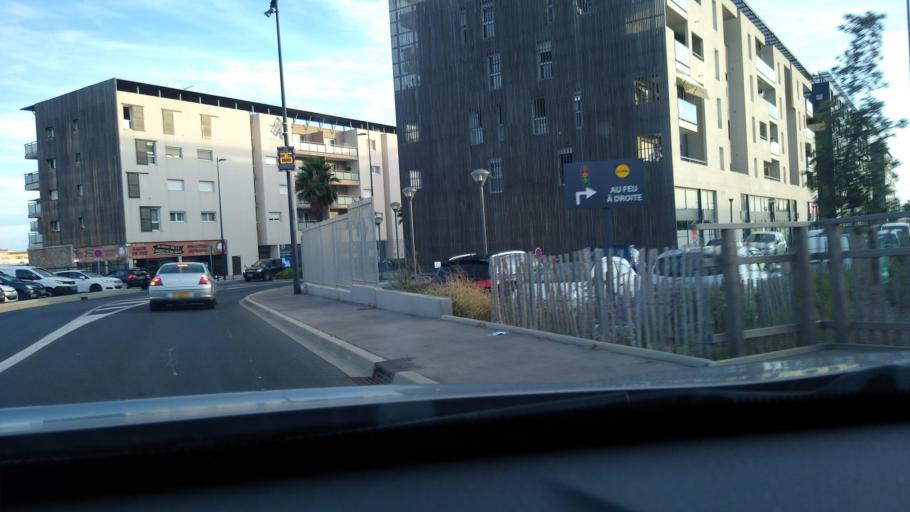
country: FR
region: Languedoc-Roussillon
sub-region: Departement de l'Herault
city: Sete
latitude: 43.4000
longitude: 3.6588
